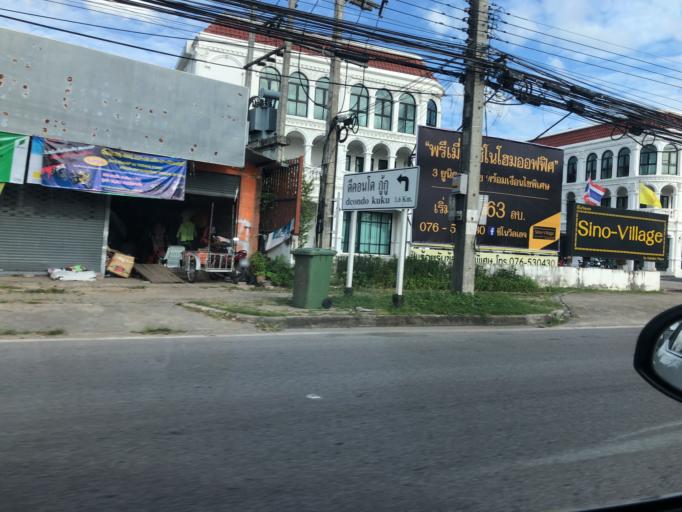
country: TH
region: Phuket
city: Ban Ratsada
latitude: 7.9114
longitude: 98.3927
